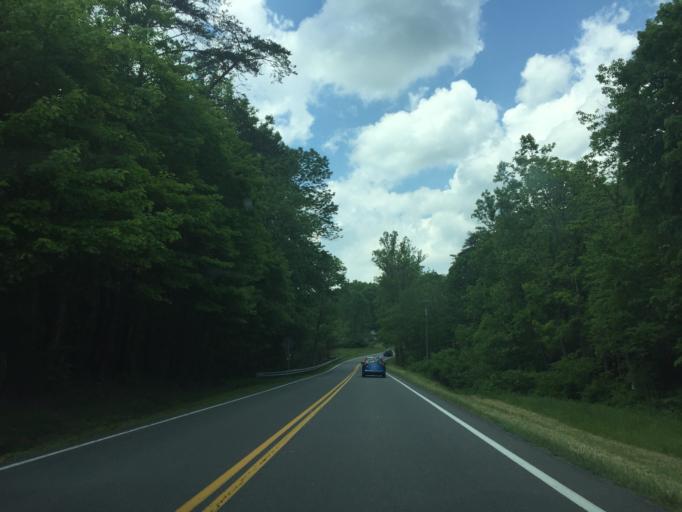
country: US
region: Virginia
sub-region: Shenandoah County
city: Strasburg
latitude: 39.0890
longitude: -78.4359
